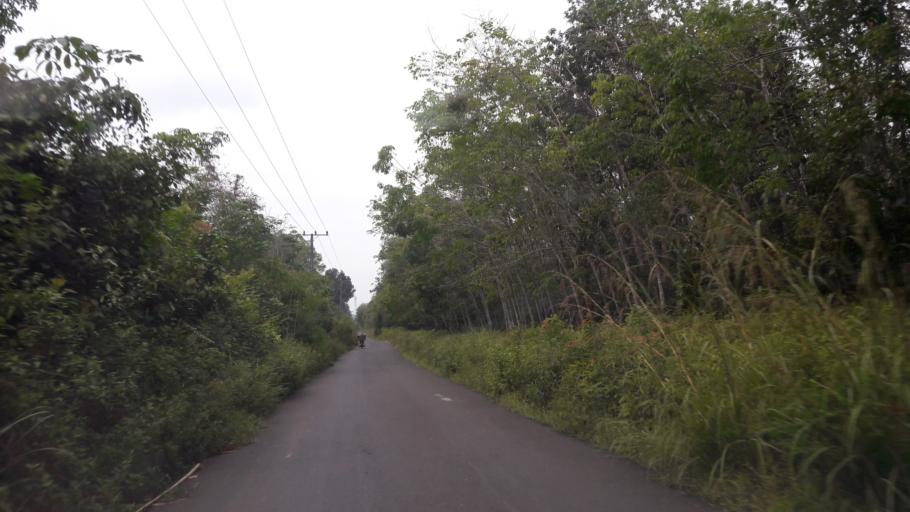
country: ID
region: South Sumatra
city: Gunungmenang
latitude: -3.2190
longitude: 104.0417
